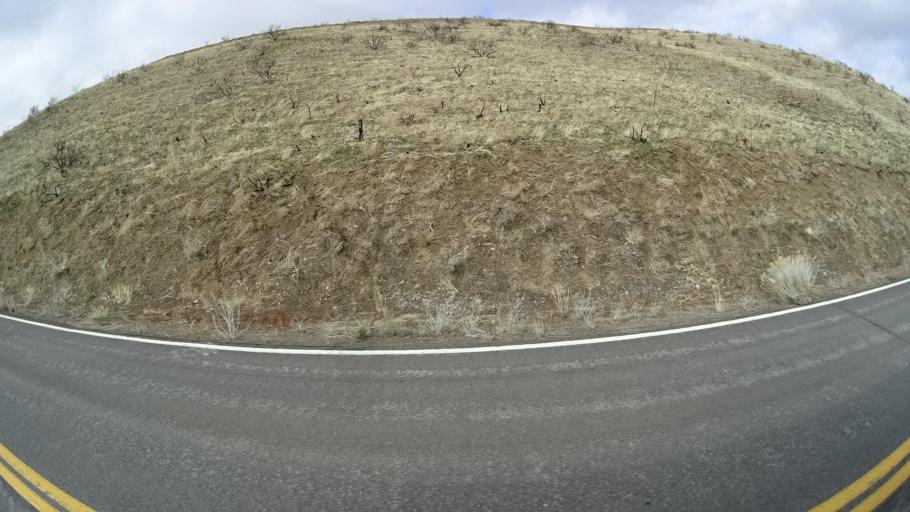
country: US
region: Nevada
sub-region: Washoe County
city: Cold Springs
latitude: 39.8407
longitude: -119.9351
